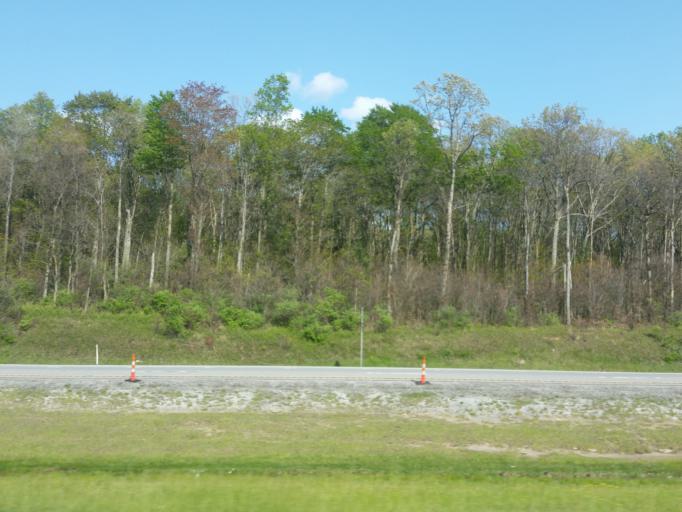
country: US
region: West Virginia
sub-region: Raleigh County
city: Shady Spring
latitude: 37.6111
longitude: -81.1211
